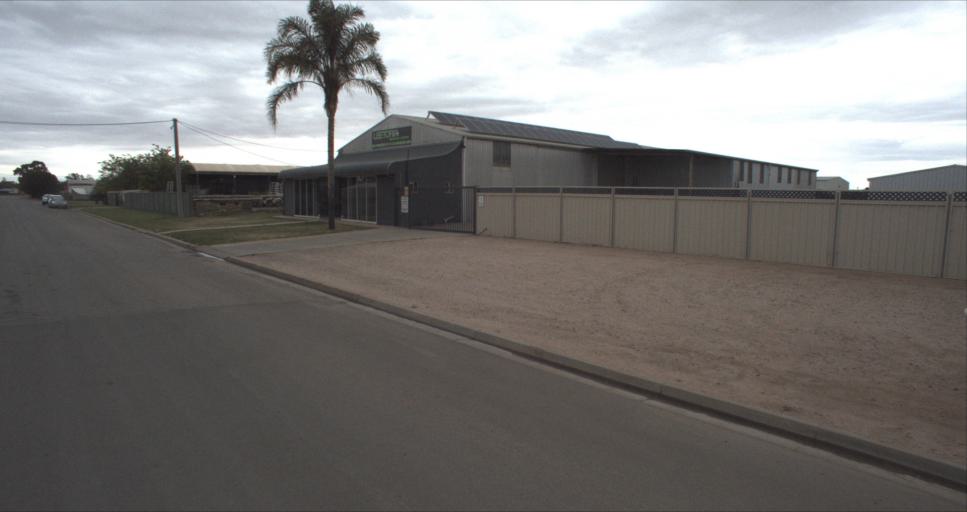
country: AU
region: New South Wales
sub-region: Leeton
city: Leeton
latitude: -34.5473
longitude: 146.3909
